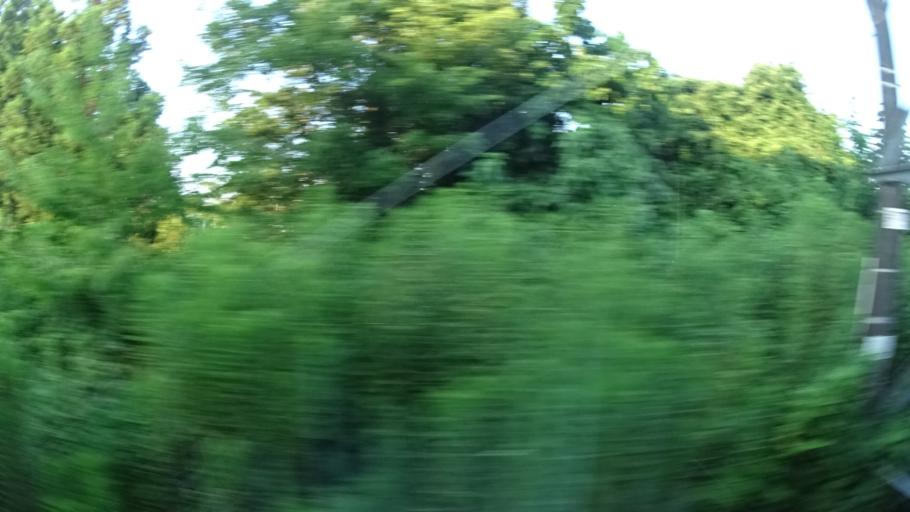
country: JP
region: Ibaraki
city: Ishioka
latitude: 36.1879
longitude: 140.2820
